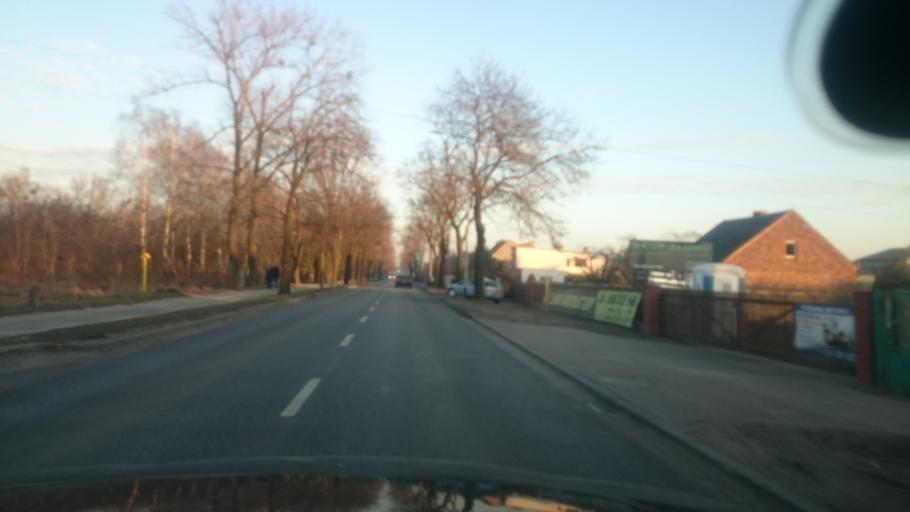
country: PL
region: Greater Poland Voivodeship
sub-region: Powiat ostrowski
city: Ostrow Wielkopolski
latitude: 51.6471
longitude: 17.8516
